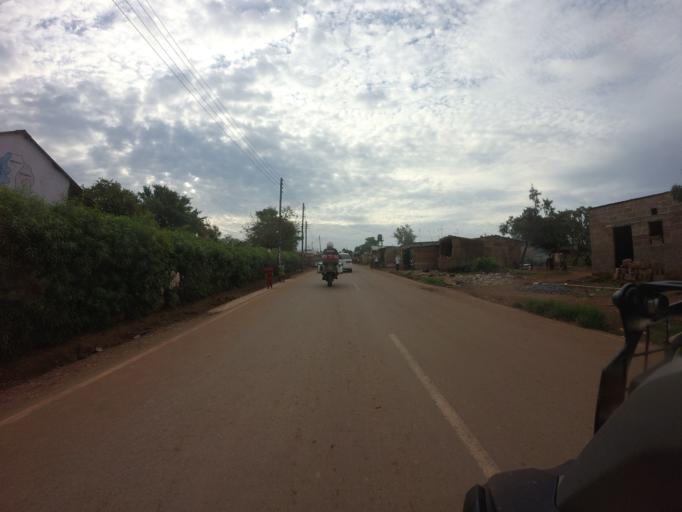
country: ZM
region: Lusaka
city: Lusaka
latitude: -15.5403
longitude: 28.2383
